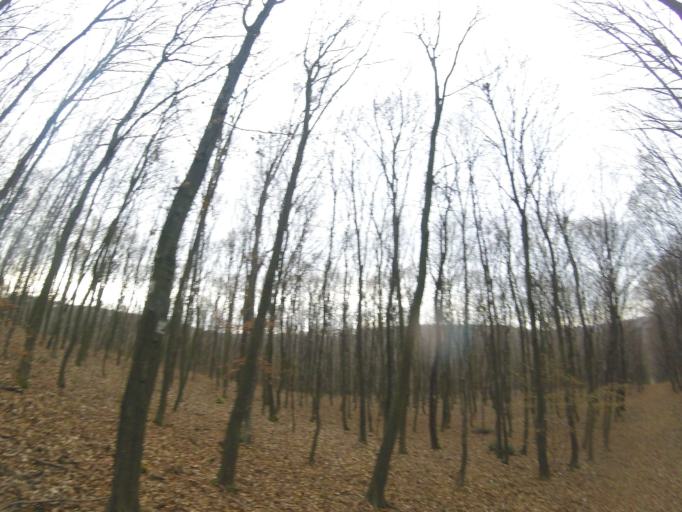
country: HU
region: Tolna
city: Szentgalpuszta
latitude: 46.3284
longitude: 18.6311
